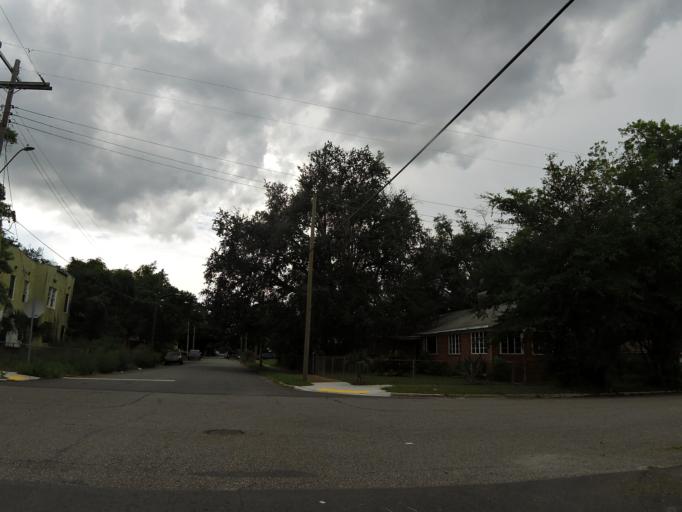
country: US
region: Florida
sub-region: Duval County
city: Jacksonville
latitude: 30.3550
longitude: -81.6553
